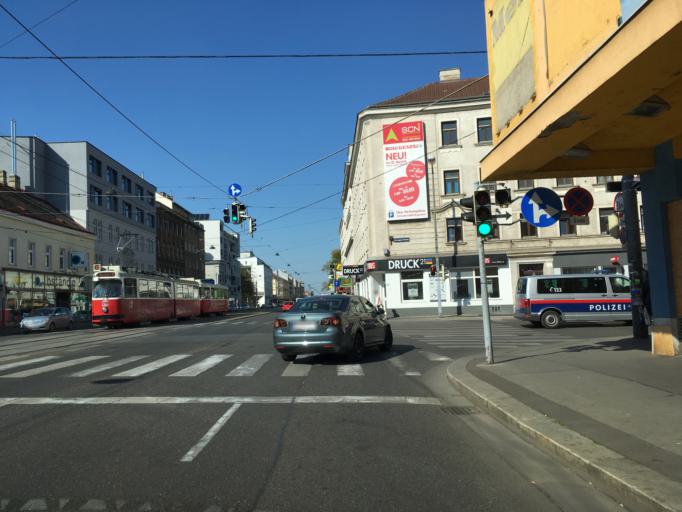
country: AT
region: Vienna
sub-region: Wien Stadt
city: Vienna
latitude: 48.2597
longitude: 16.3991
